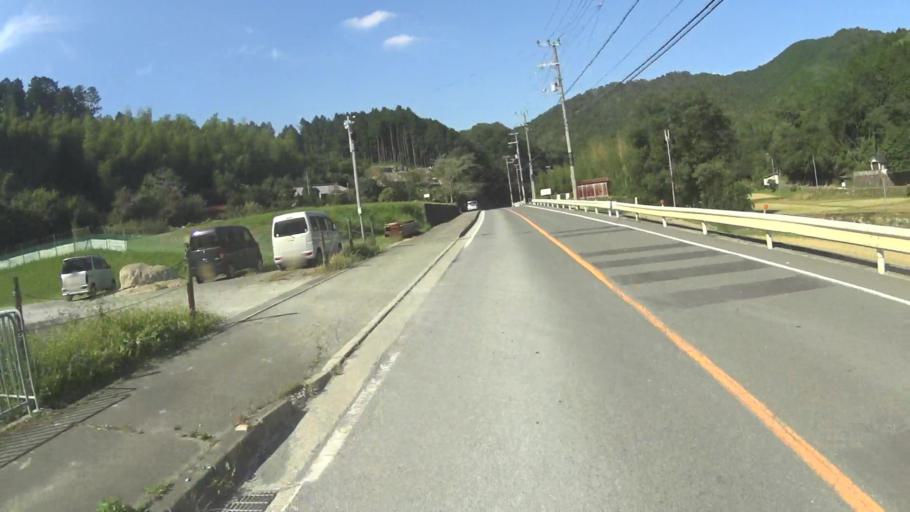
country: JP
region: Kyoto
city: Kameoka
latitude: 34.9349
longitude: 135.5558
